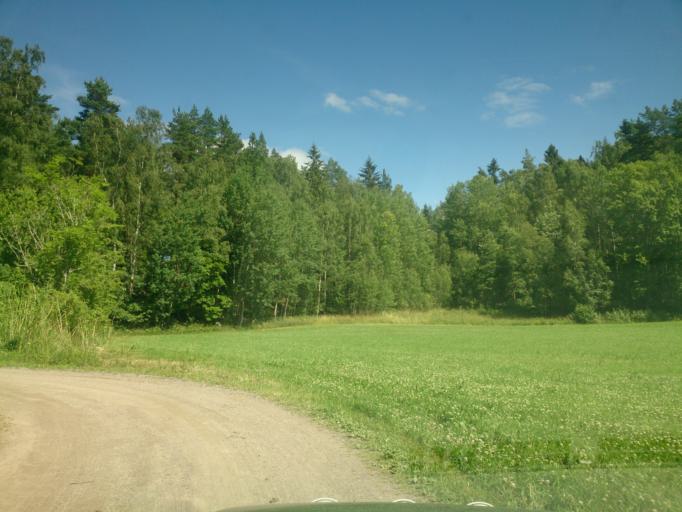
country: SE
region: OEstergoetland
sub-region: Atvidabergs Kommun
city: Atvidaberg
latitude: 58.2395
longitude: 15.9634
